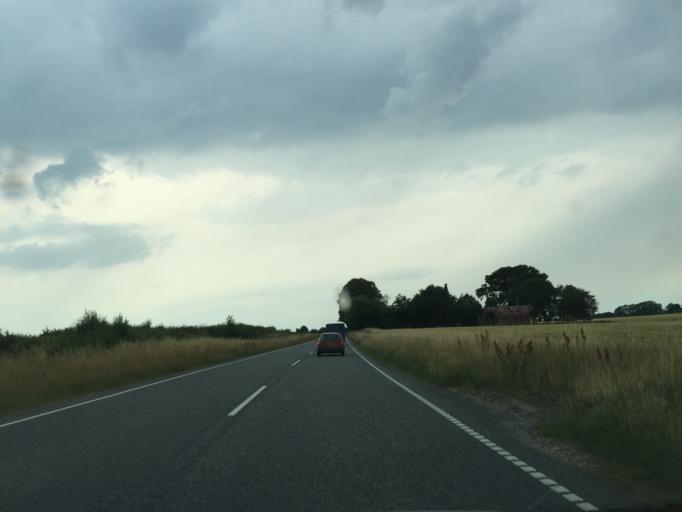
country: DK
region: Central Jutland
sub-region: Silkeborg Kommune
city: Kjellerup
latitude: 56.2975
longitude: 9.4497
